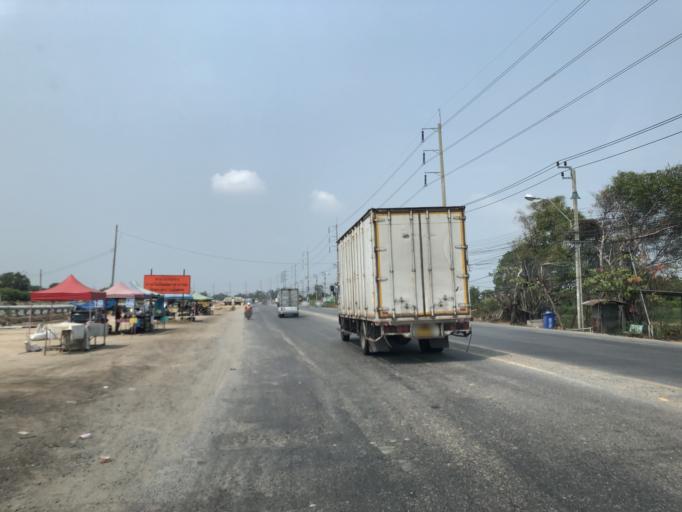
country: TH
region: Samut Prakan
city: Bang Bo District
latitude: 13.5121
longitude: 100.7927
